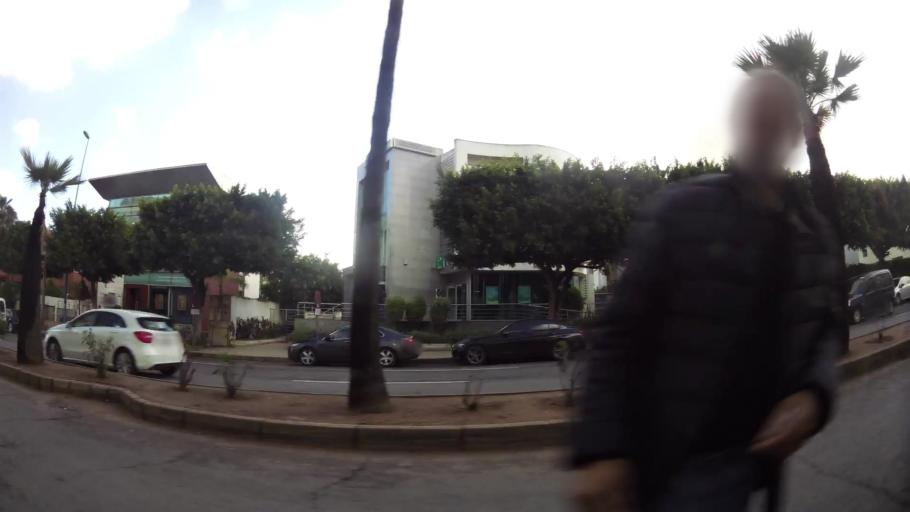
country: MA
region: Grand Casablanca
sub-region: Casablanca
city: Casablanca
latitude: 33.5549
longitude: -7.6238
